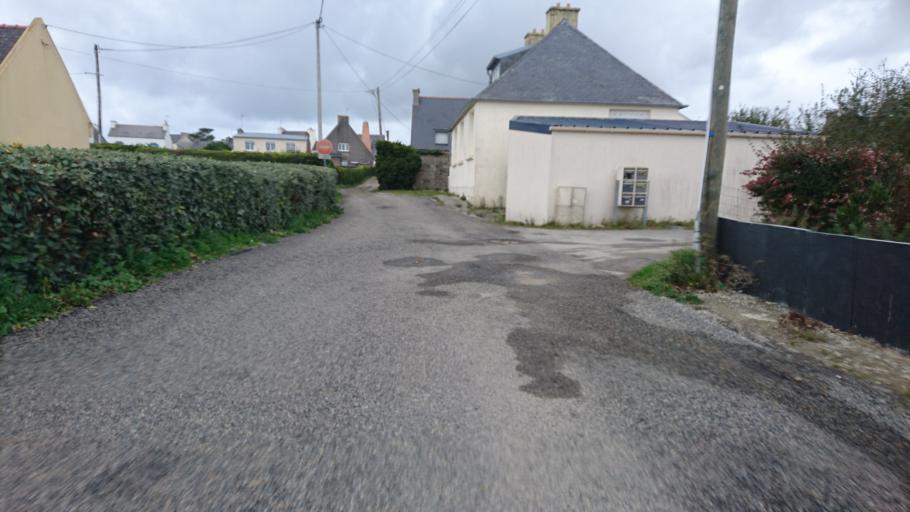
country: FR
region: Brittany
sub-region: Departement du Finistere
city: Lampaul-Plouarzel
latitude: 48.4477
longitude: -4.7648
